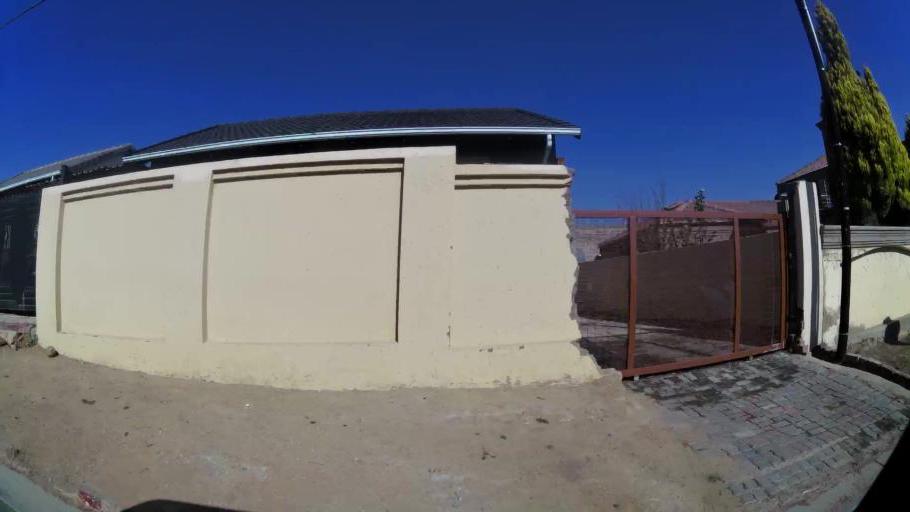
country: ZA
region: Gauteng
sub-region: West Rand District Municipality
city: Muldersdriseloop
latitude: -26.0381
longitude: 27.9194
